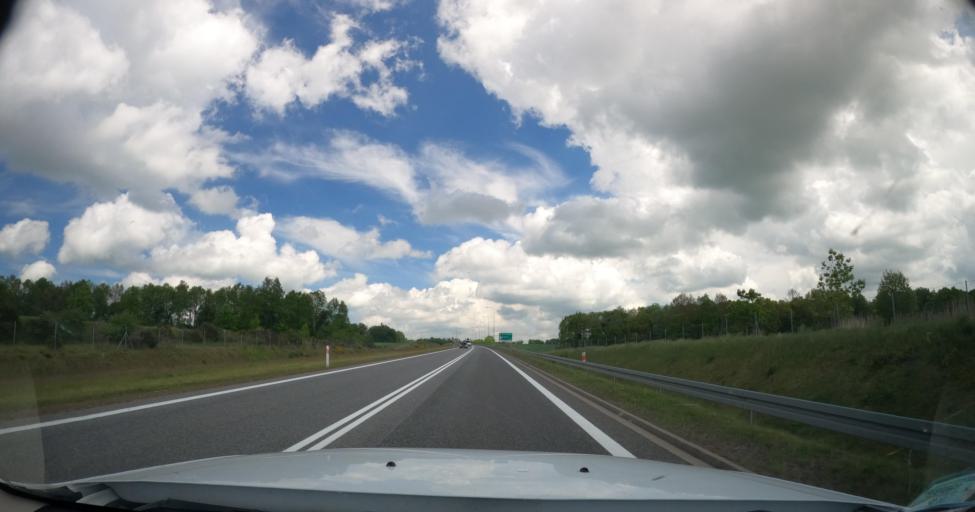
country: PL
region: Pomeranian Voivodeship
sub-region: Slupsk
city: Slupsk
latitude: 54.4627
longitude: 17.1104
